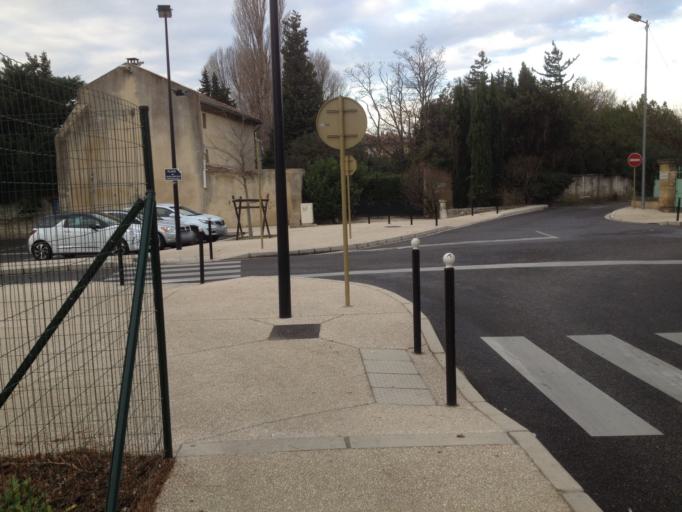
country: FR
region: Provence-Alpes-Cote d'Azur
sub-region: Departement du Vaucluse
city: Orange
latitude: 44.1387
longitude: 4.8034
